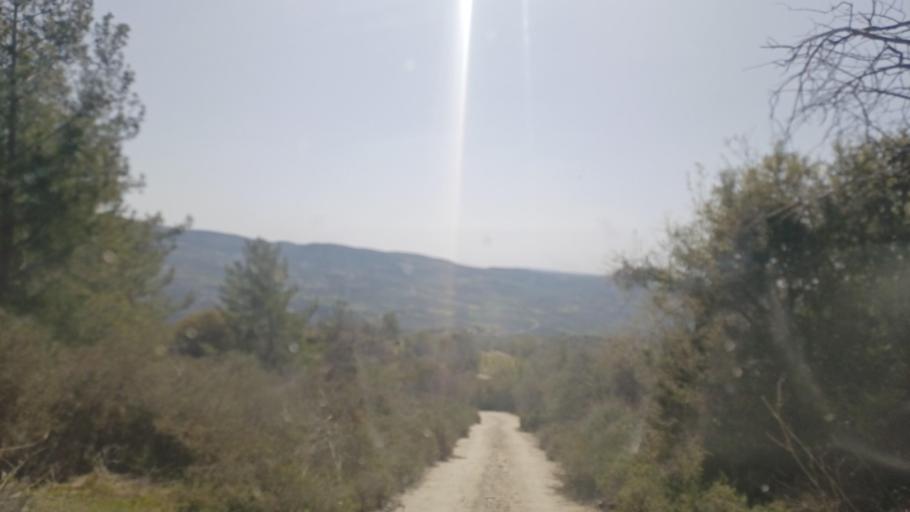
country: CY
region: Limassol
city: Pachna
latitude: 34.8714
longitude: 32.7113
